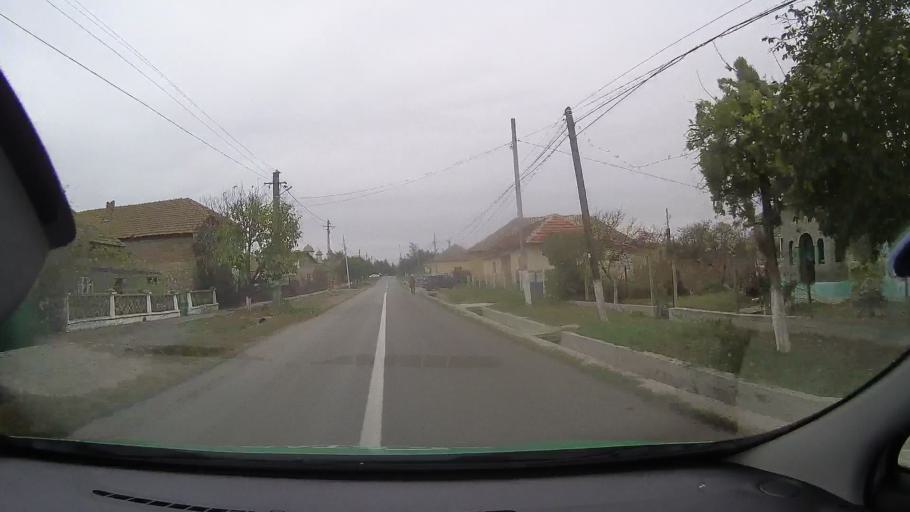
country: RO
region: Constanta
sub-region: Comuna Targusor
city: Targusor
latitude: 44.4628
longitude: 28.4199
